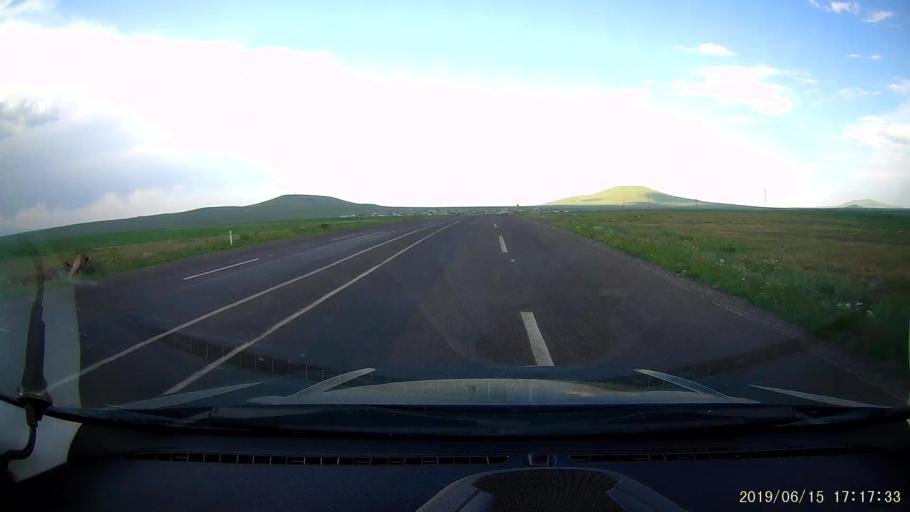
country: TR
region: Kars
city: Kars
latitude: 40.6149
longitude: 43.2412
